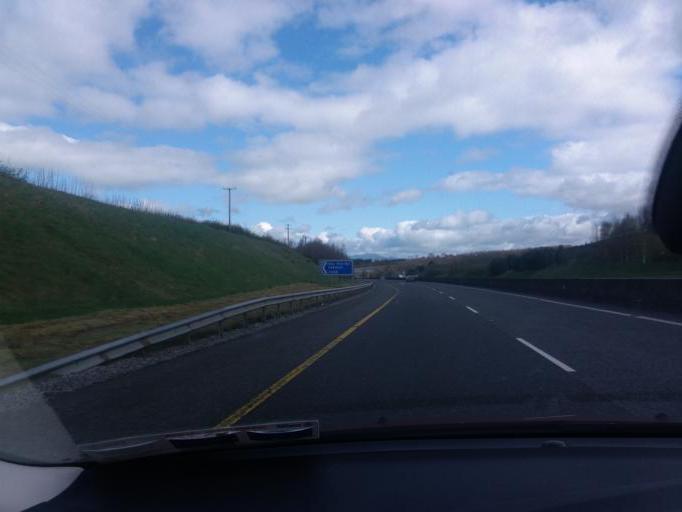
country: IE
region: Munster
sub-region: County Cork
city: Fermoy
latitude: 52.1094
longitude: -8.2743
